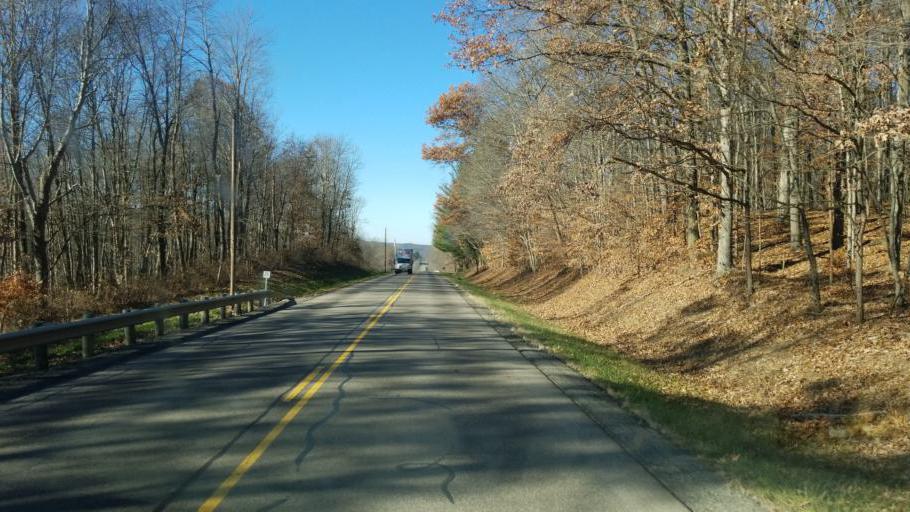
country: US
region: Ohio
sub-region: Knox County
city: Oak Hill
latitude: 40.3460
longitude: -82.2050
